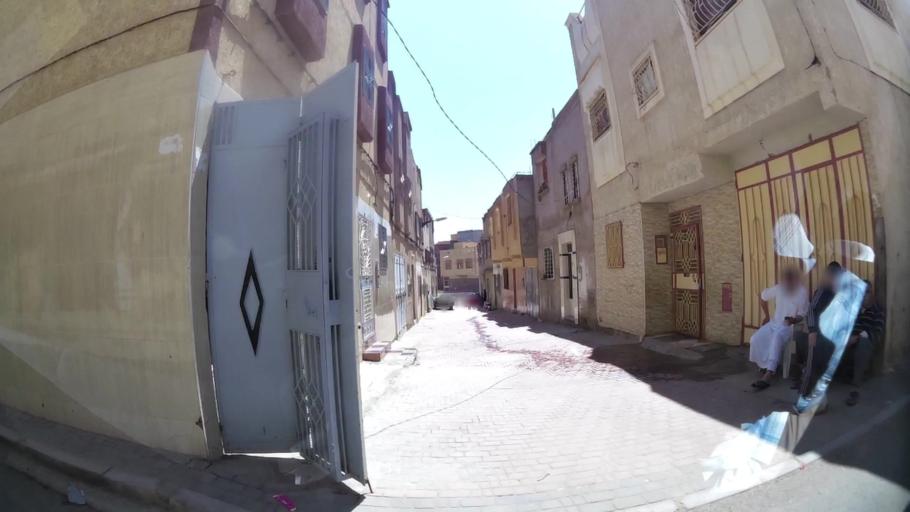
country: MA
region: Oriental
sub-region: Oujda-Angad
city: Oujda
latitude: 34.6815
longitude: -1.9551
